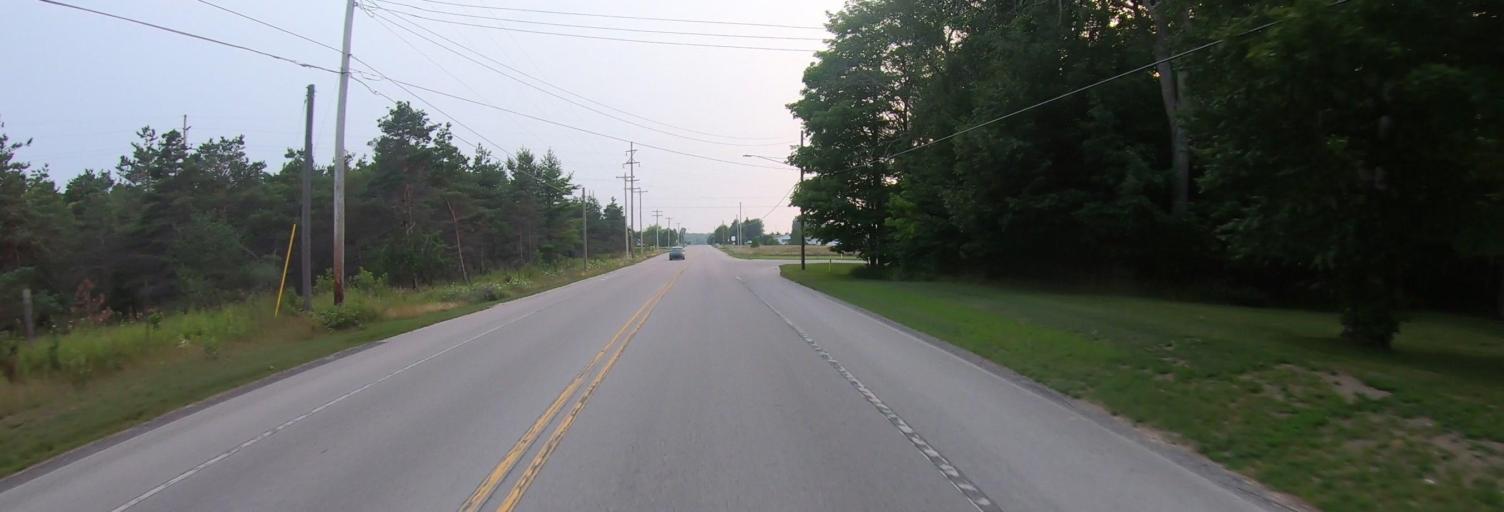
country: US
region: Michigan
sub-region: Mackinac County
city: Saint Ignace
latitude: 45.7818
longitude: -84.7595
